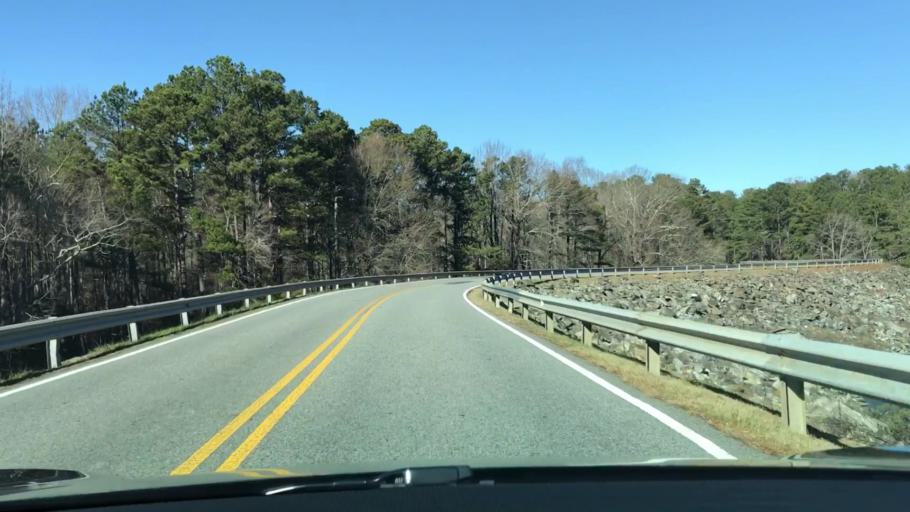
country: US
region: Georgia
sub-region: Forsyth County
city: Cumming
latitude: 34.1713
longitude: -84.0781
